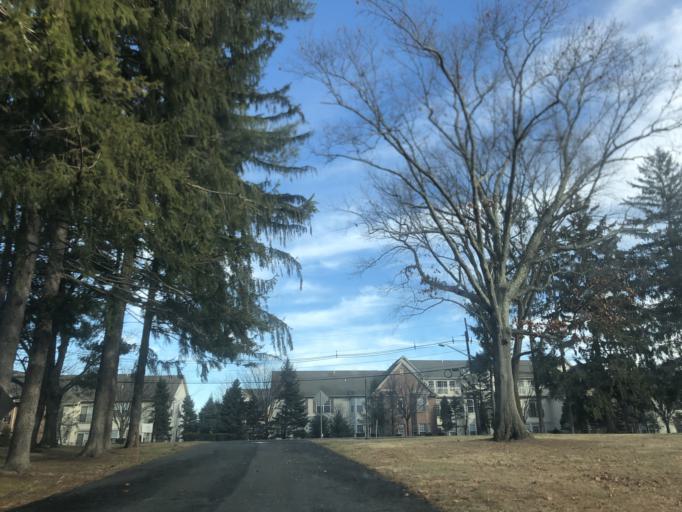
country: US
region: New Jersey
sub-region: Somerset County
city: Kingston
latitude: 40.3589
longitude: -74.6193
